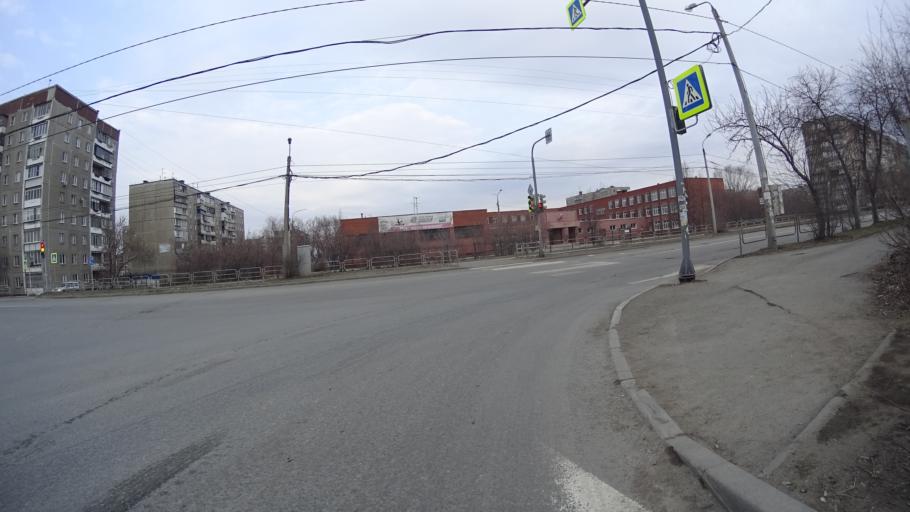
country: RU
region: Chelyabinsk
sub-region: Gorod Chelyabinsk
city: Chelyabinsk
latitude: 55.1910
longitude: 61.4820
